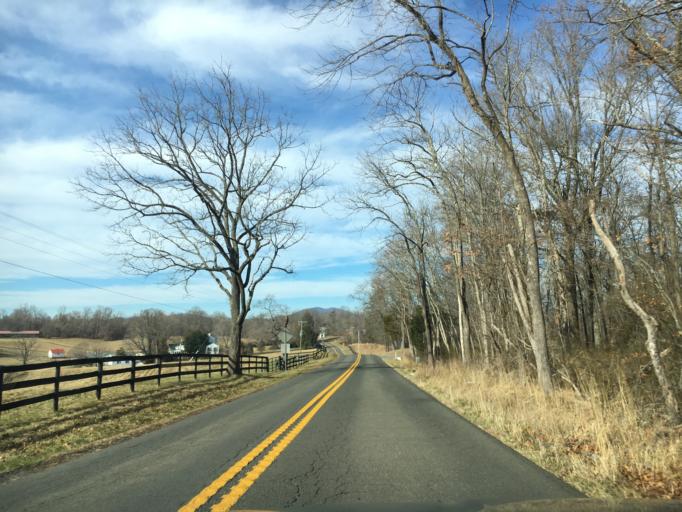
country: US
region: Virginia
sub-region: Fauquier County
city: Marshall
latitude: 38.7782
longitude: -77.9811
